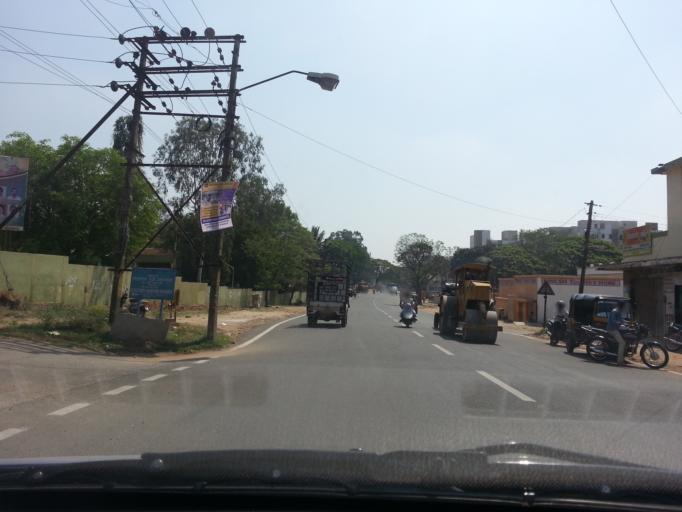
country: IN
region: Karnataka
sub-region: Mysore
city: Mysore
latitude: 12.3081
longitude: 76.6741
